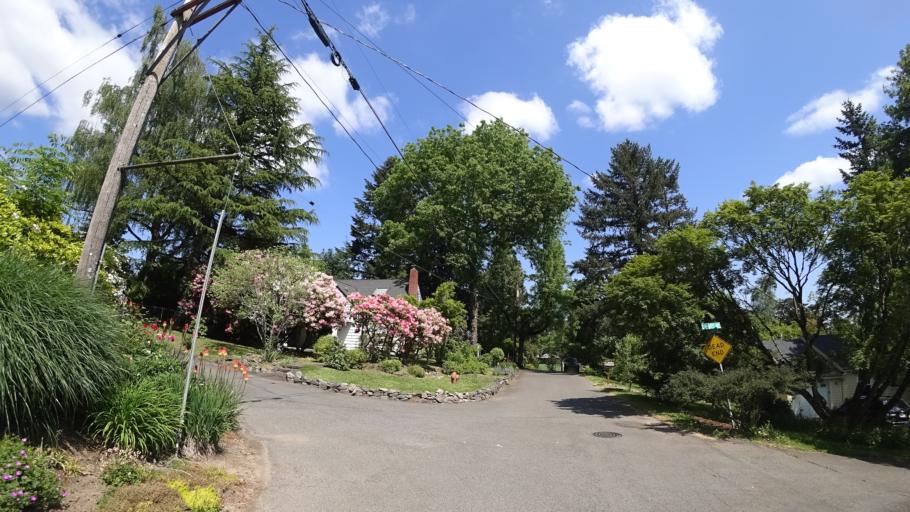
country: US
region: Oregon
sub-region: Washington County
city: Garden Home-Whitford
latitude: 45.4672
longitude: -122.7043
